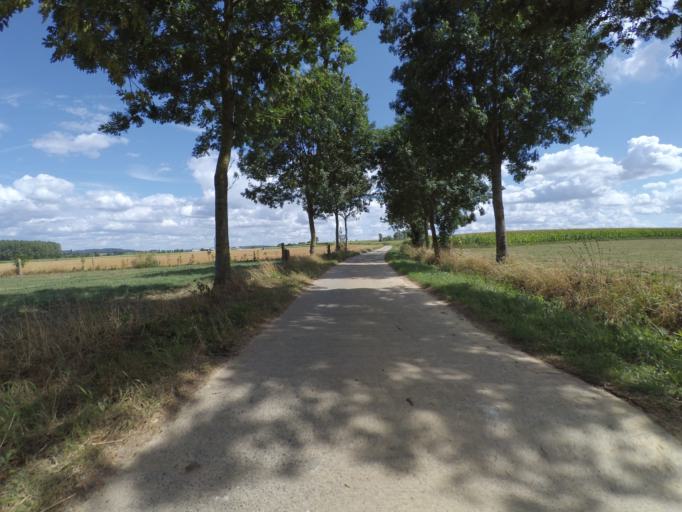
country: BE
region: Wallonia
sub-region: Province du Hainaut
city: Frasnes-lez-Buissenal
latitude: 50.6658
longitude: 3.5935
